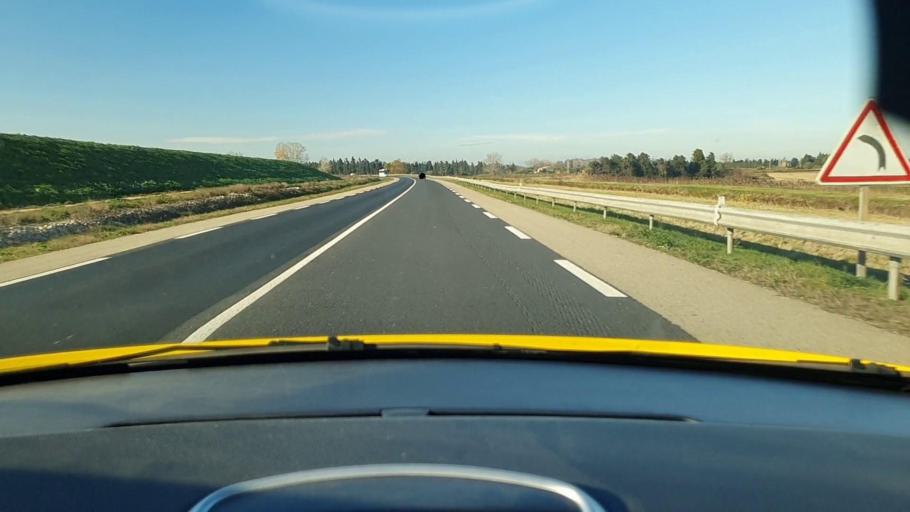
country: FR
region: Languedoc-Roussillon
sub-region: Departement du Gard
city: Fourques
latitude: 43.6968
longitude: 4.5863
